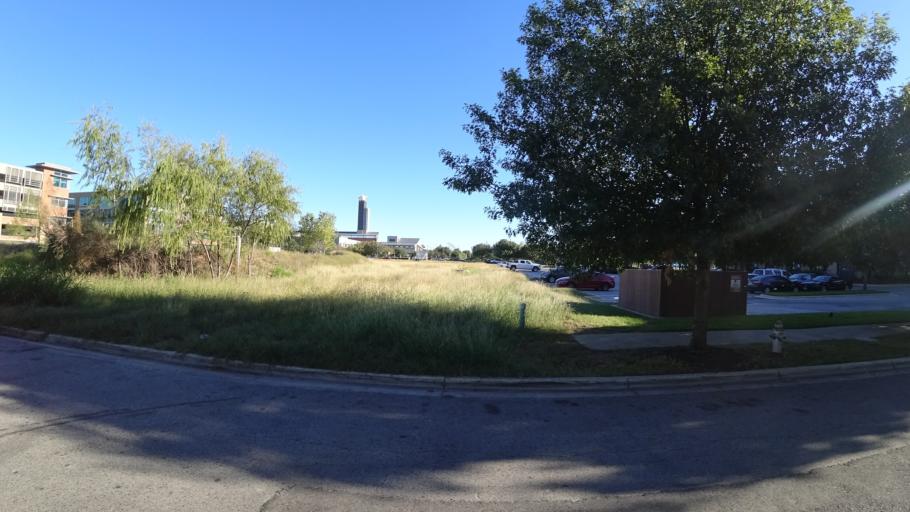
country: US
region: Texas
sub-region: Travis County
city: Austin
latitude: 30.3007
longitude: -97.7073
